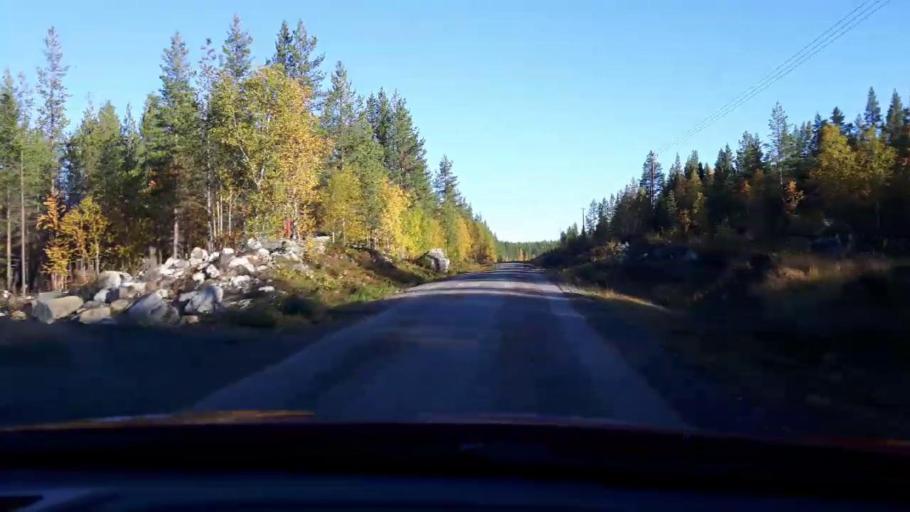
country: SE
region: Jaemtland
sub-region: Stroemsunds Kommun
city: Stroemsund
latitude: 64.3753
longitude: 15.1510
